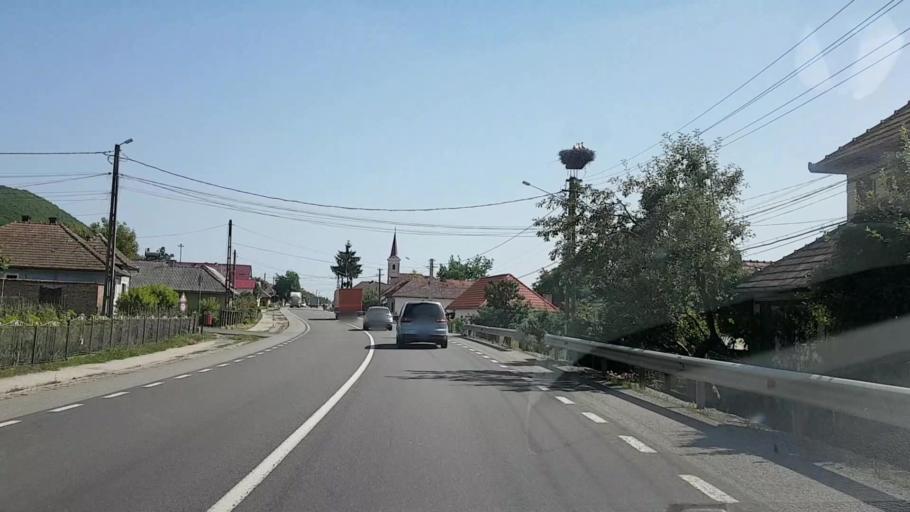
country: RO
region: Bistrita-Nasaud
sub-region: Comuna Sieu-Odorhei
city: Sieu-Odorhei
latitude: 47.1488
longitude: 24.3057
